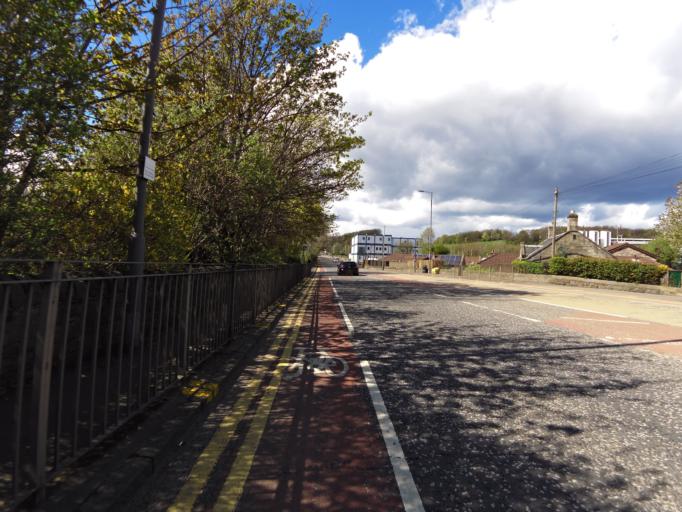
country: GB
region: Scotland
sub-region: Midlothian
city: Loanhead
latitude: 55.9197
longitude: -3.1382
